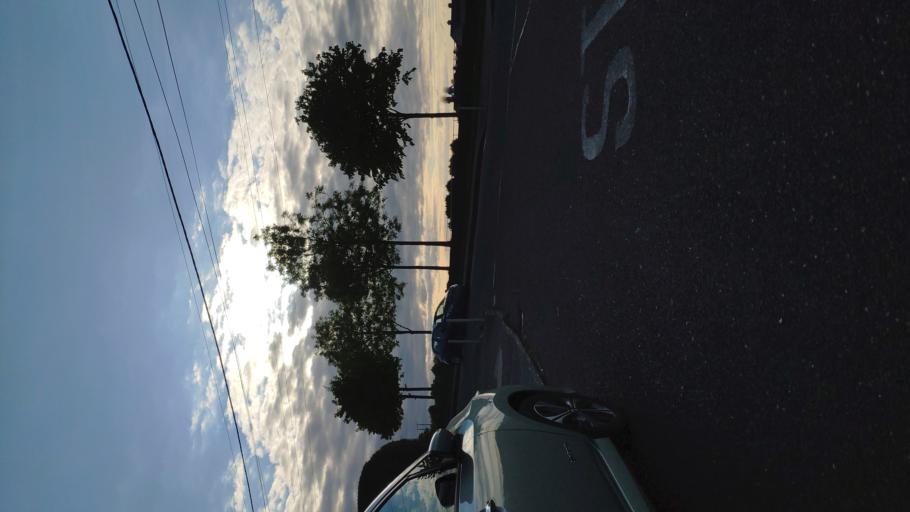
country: IE
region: Munster
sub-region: County Cork
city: Cork
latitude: 51.9156
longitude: -8.4870
